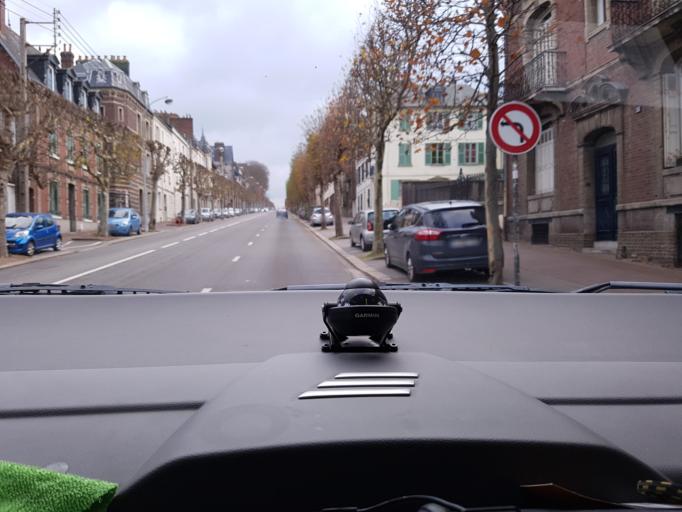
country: FR
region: Haute-Normandie
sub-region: Departement de la Seine-Maritime
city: Dieppe
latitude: 49.9210
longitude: 1.0734
